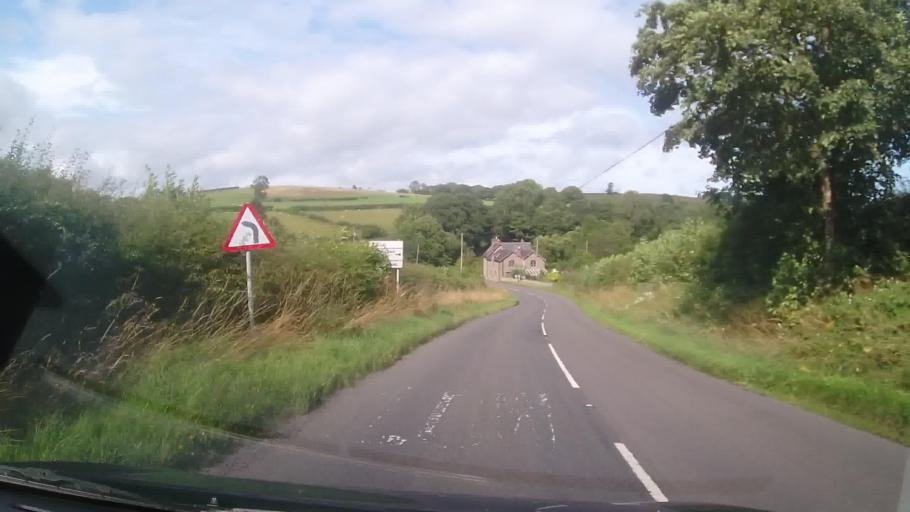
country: GB
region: Wales
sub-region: Sir Powys
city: Knighton
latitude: 52.3829
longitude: -3.0394
